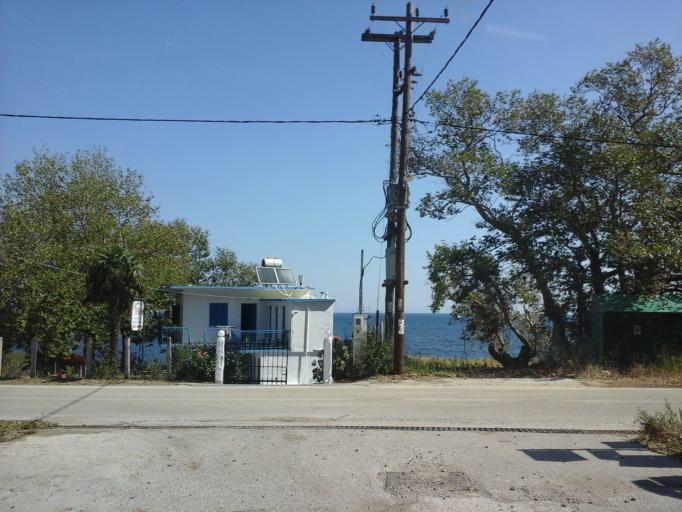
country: GR
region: East Macedonia and Thrace
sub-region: Nomos Evrou
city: Samothraki
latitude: 40.5085
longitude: 25.5704
